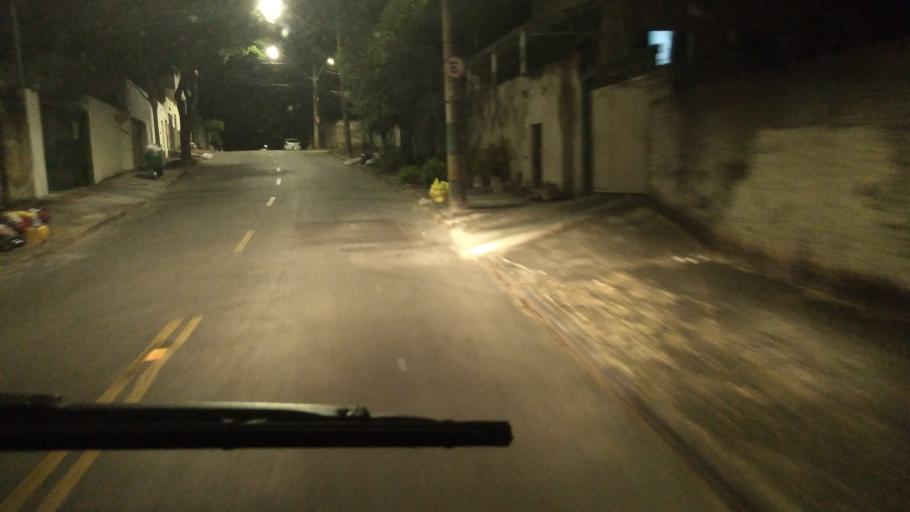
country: BR
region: Minas Gerais
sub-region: Belo Horizonte
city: Belo Horizonte
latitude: -19.8768
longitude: -43.9377
